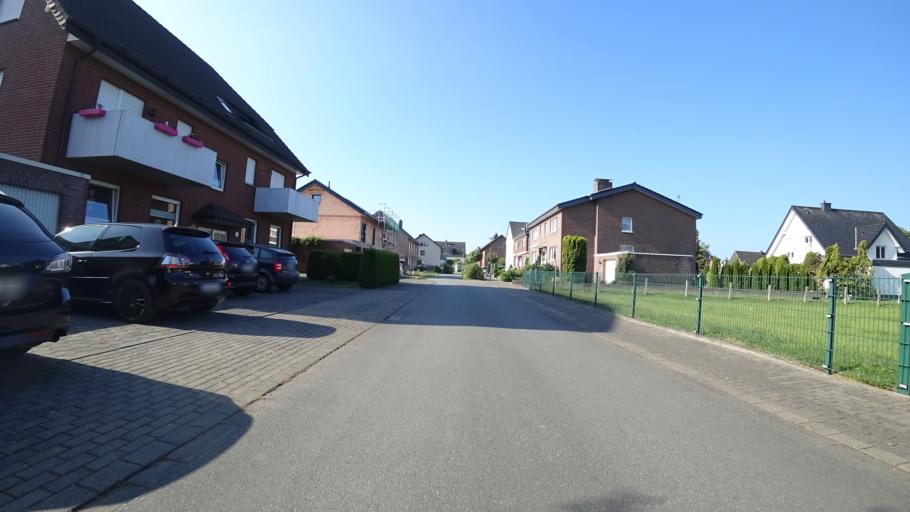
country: DE
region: North Rhine-Westphalia
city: Erwitte
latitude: 51.6343
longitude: 8.3663
